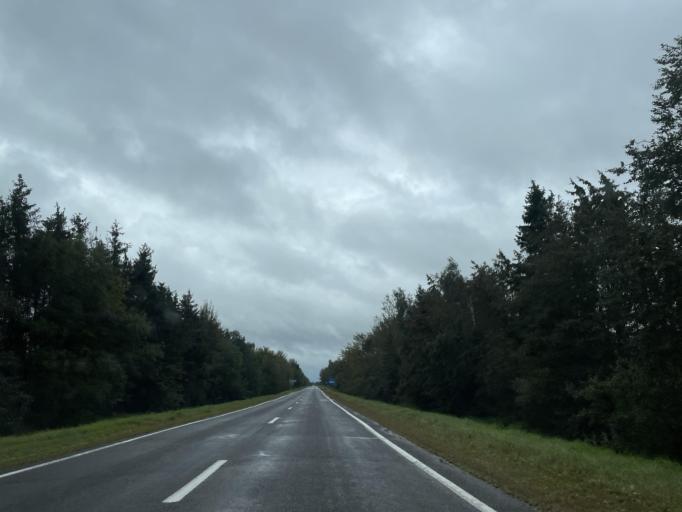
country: BY
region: Minsk
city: Snow
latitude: 53.1906
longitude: 26.2797
